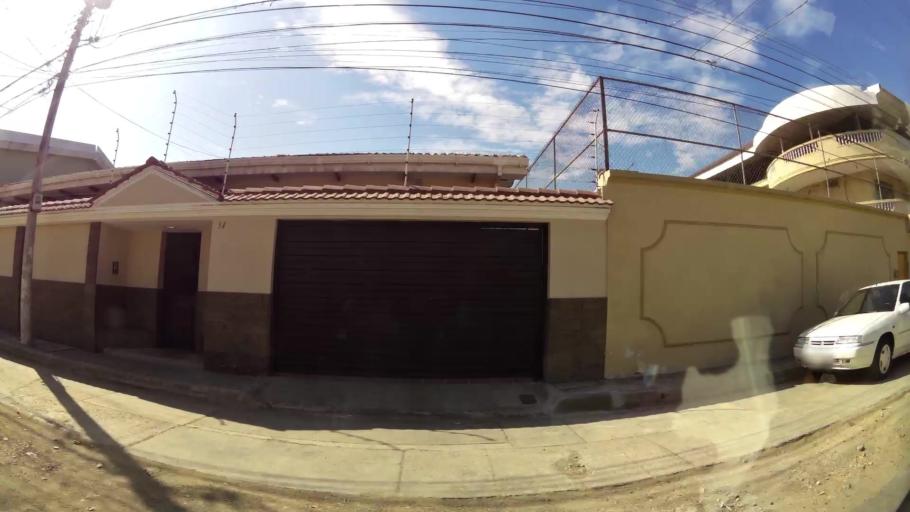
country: EC
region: Guayas
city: Guayaquil
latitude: -2.2293
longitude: -79.8929
